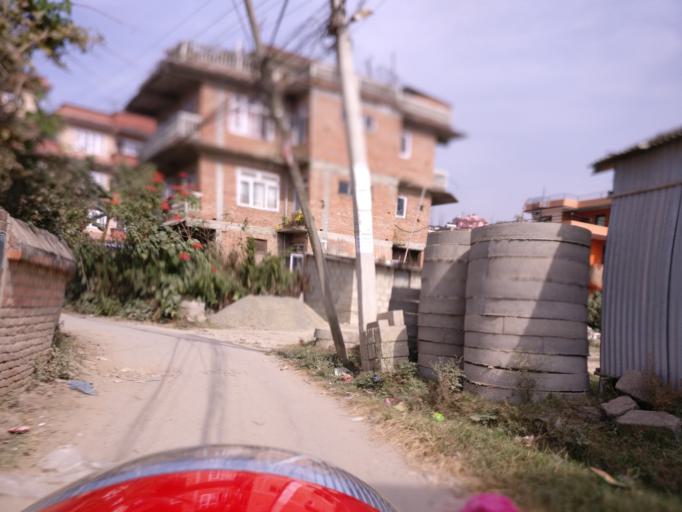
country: NP
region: Central Region
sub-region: Bagmati Zone
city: Patan
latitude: 27.6573
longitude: 85.3130
